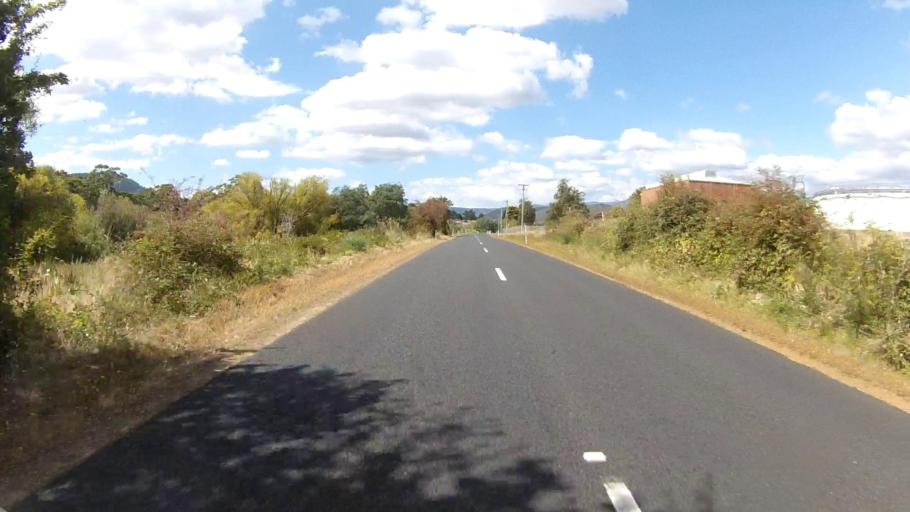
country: AU
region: Tasmania
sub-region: Derwent Valley
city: New Norfolk
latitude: -42.7662
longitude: 147.0191
